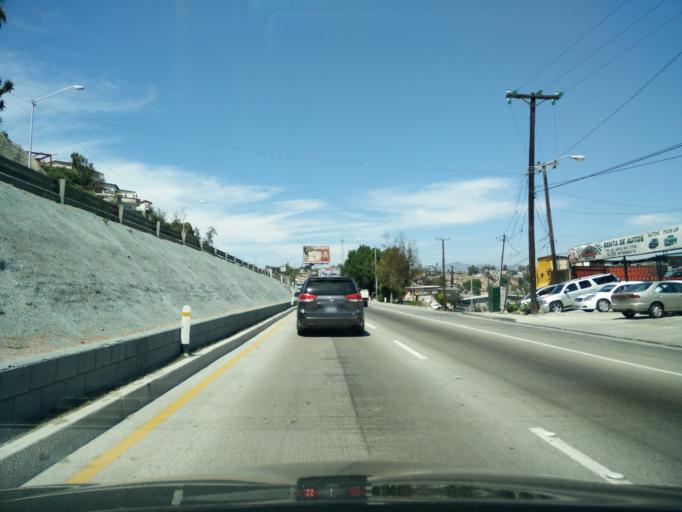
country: MX
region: Baja California
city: Tijuana
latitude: 32.5352
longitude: -116.9963
